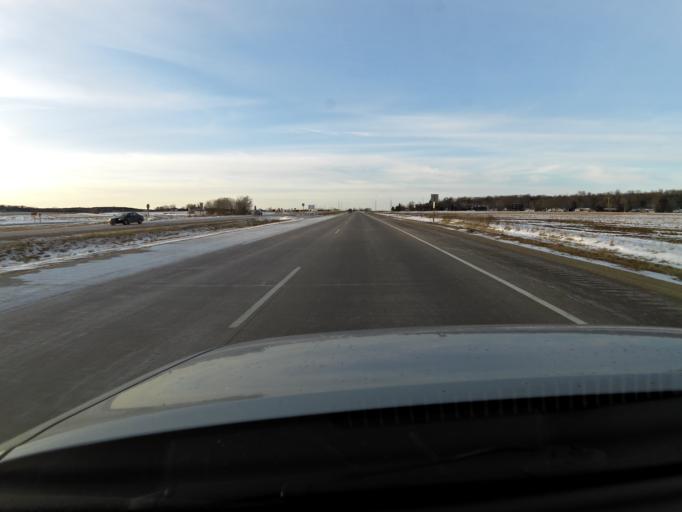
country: US
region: Wisconsin
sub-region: Pierce County
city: River Falls
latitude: 44.9089
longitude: -92.6608
